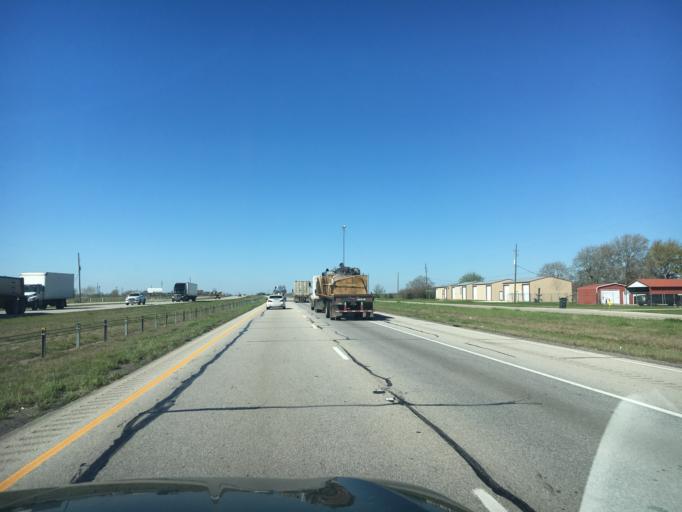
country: US
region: Texas
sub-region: Austin County
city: Sealy
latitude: 29.7513
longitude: -96.2809
